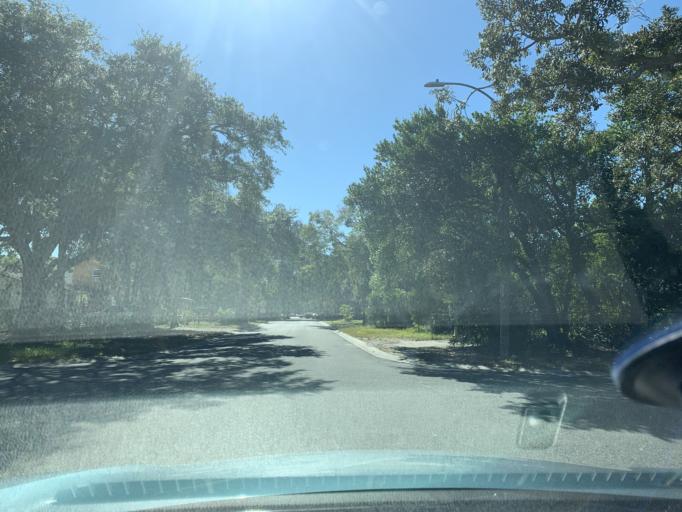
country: US
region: Florida
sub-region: Pinellas County
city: Gulfport
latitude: 27.7502
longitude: -82.6911
